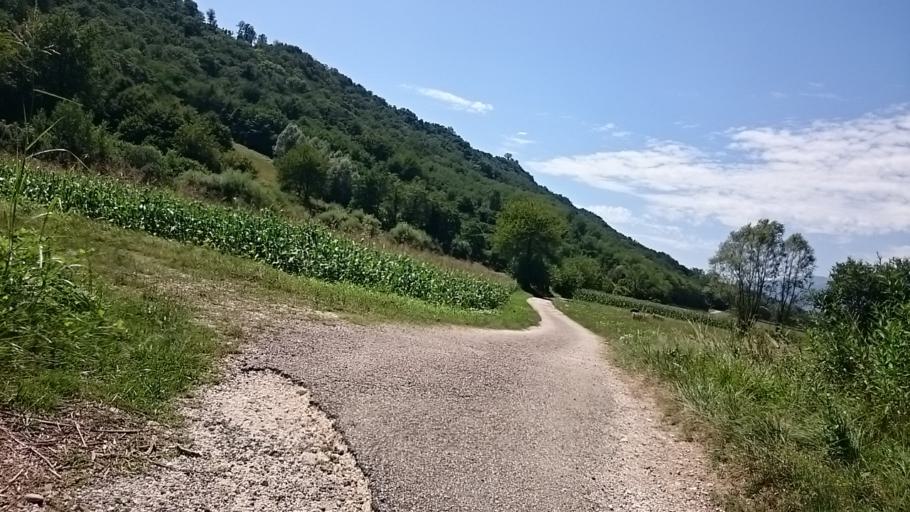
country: IT
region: Veneto
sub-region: Provincia di Treviso
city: Tarzo
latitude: 45.9748
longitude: 12.2083
